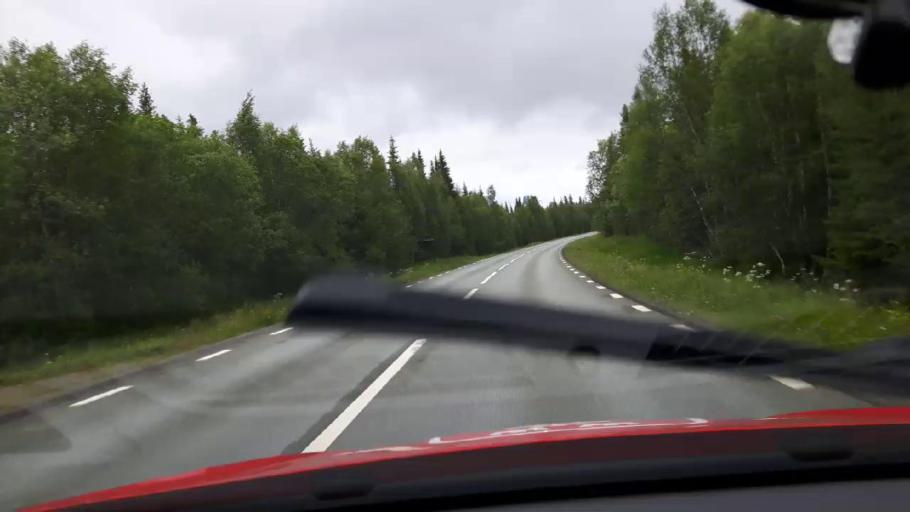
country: SE
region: Jaemtland
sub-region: Are Kommun
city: Are
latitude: 63.3328
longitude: 12.5583
